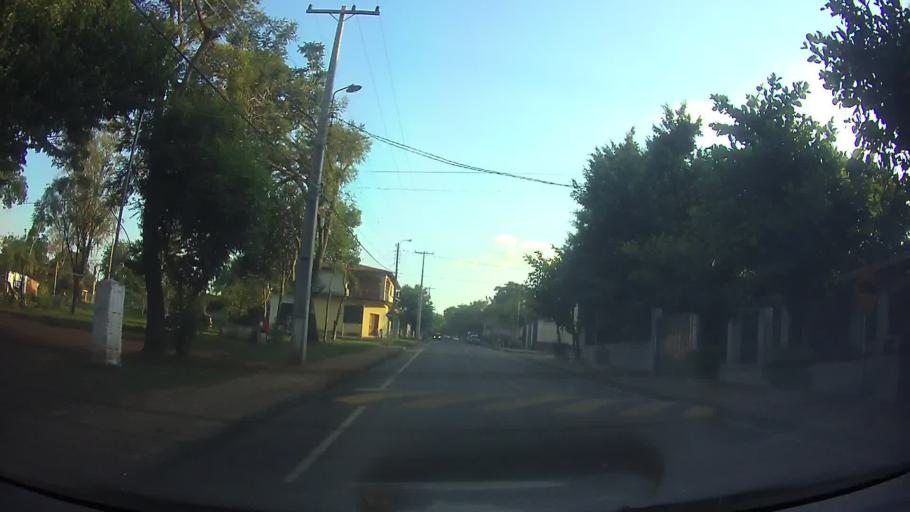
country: PY
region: Central
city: Limpio
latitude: -25.2516
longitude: -57.4984
